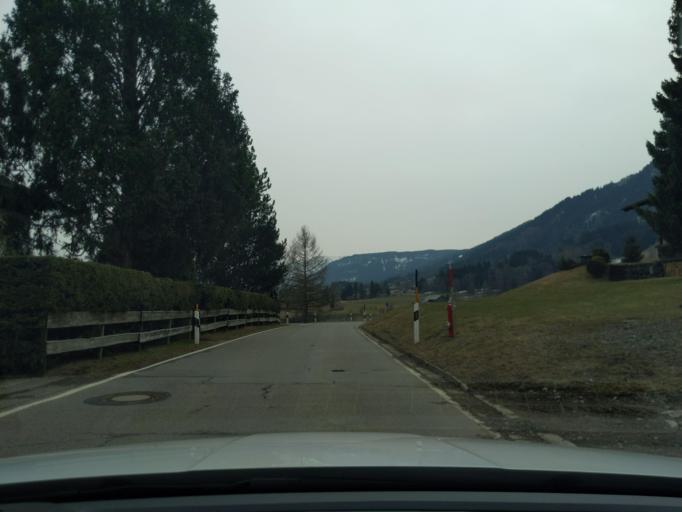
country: DE
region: Bavaria
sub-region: Swabia
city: Ofterschwang
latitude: 47.4881
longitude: 10.2343
